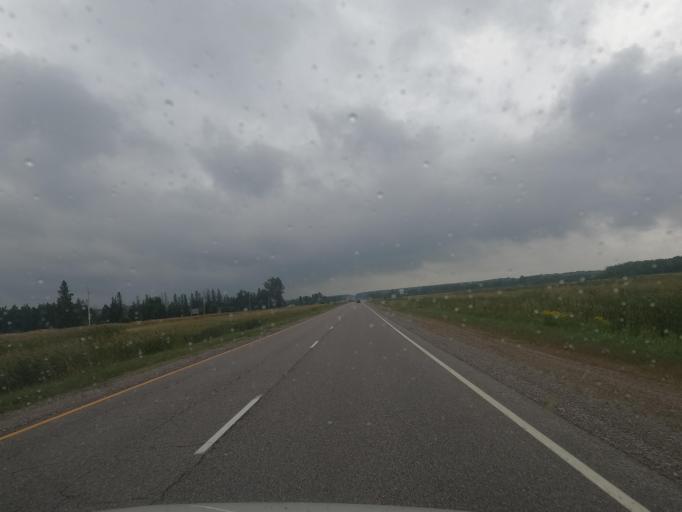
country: CA
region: Ontario
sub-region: Algoma
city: Sault Ste. Marie
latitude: 46.4402
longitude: -84.0683
